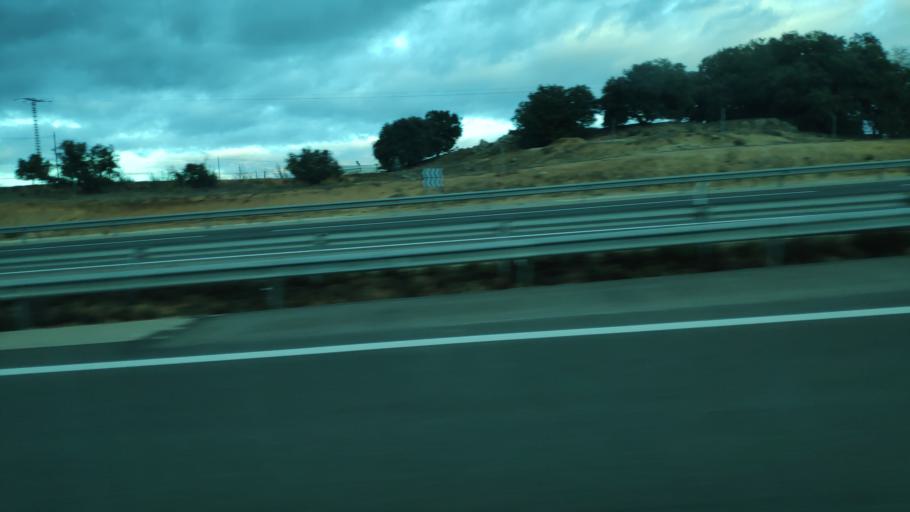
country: ES
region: Castille-La Mancha
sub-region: Provincia de Cuenca
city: Tarancon
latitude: 40.0130
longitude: -3.0301
